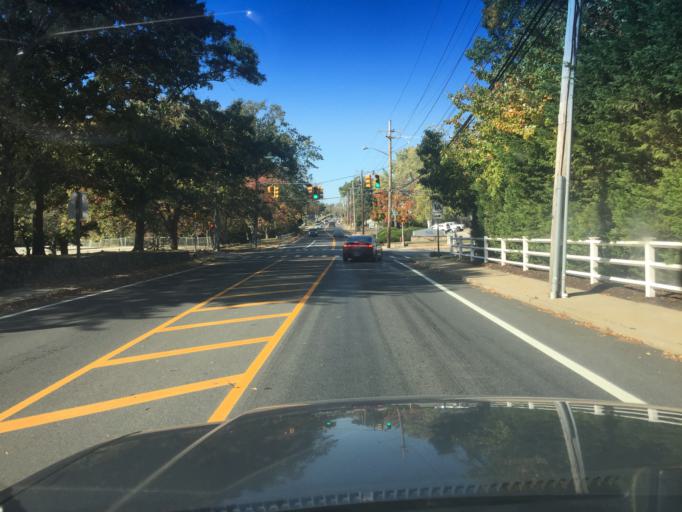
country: US
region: Rhode Island
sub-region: Providence County
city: Pawtucket
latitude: 41.8542
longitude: -71.3612
